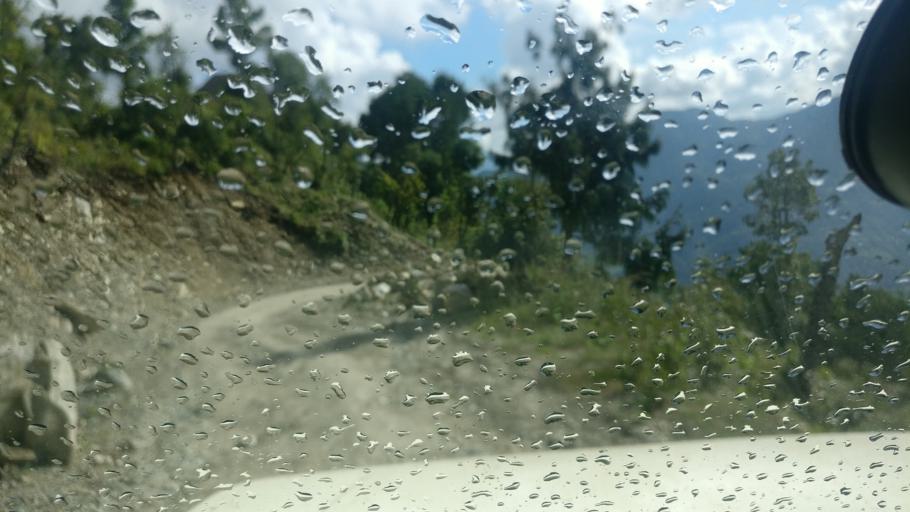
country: NP
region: Western Region
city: Baglung
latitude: 28.2804
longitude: 83.6405
